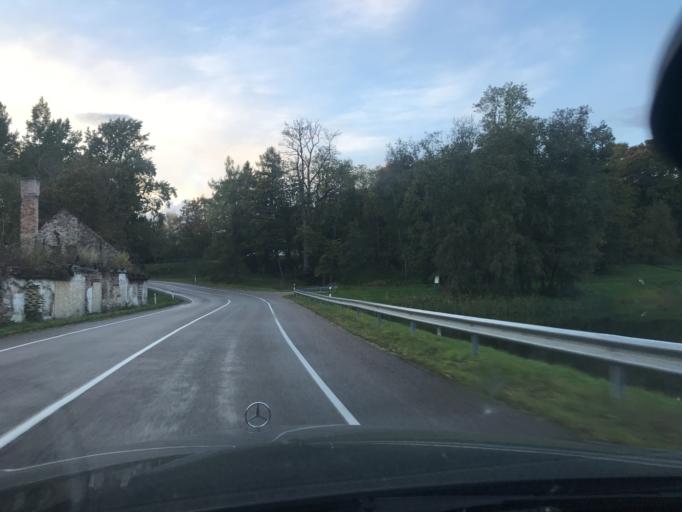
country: EE
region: Valgamaa
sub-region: Torva linn
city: Torva
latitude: 58.0082
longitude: 26.2074
